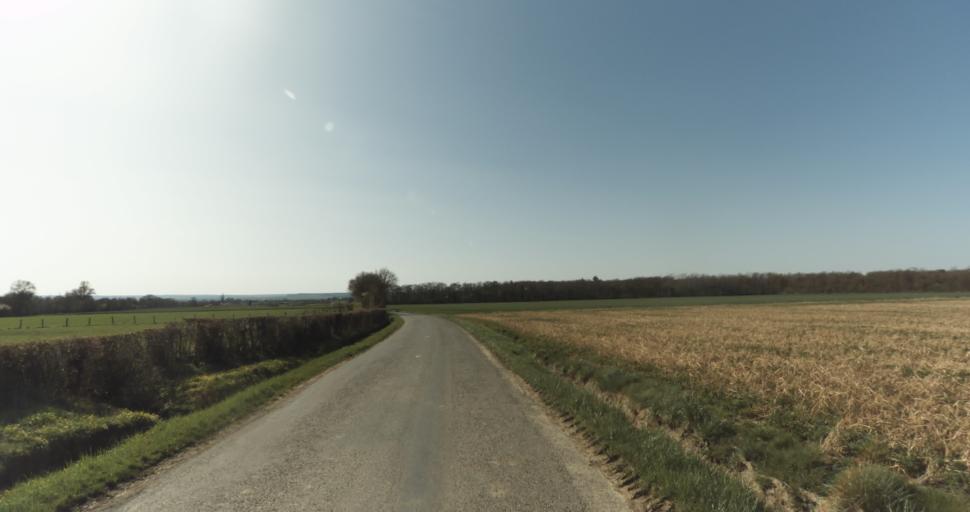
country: FR
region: Lower Normandy
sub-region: Departement du Calvados
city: Saint-Pierre-sur-Dives
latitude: 48.9409
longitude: -0.0223
